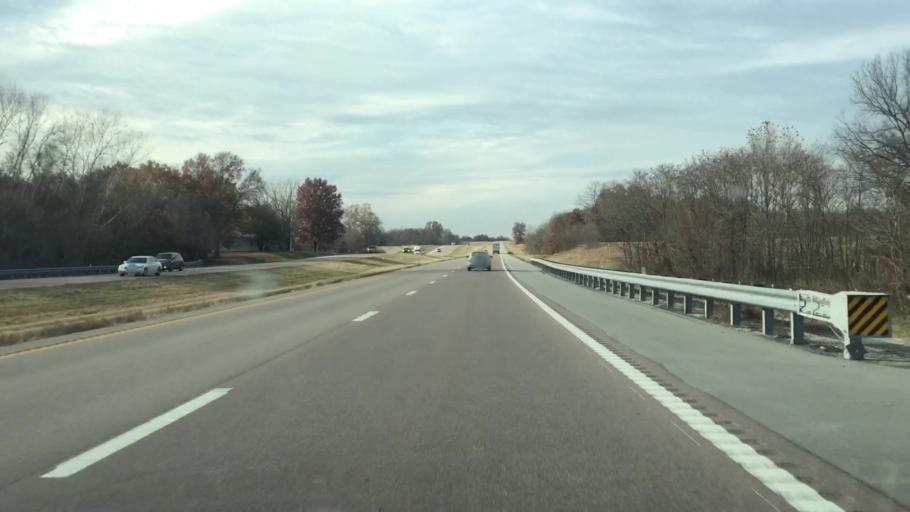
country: US
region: Missouri
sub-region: Cass County
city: Garden City
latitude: 38.4833
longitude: -94.0360
